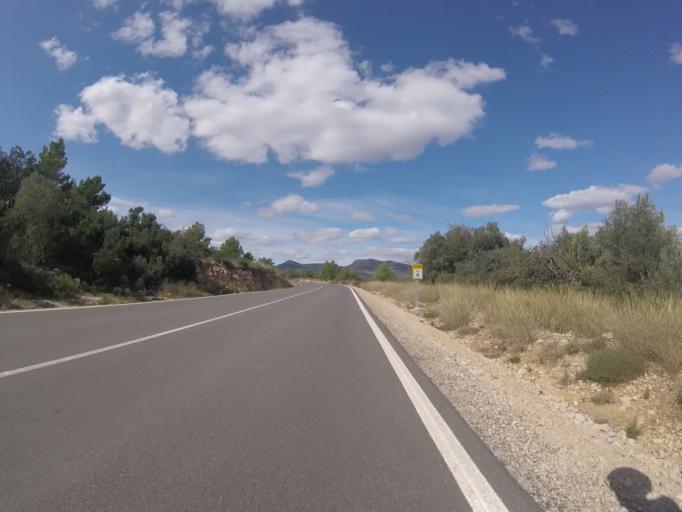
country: ES
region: Valencia
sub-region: Provincia de Castello
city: Chert/Xert
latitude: 40.4389
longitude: 0.1128
